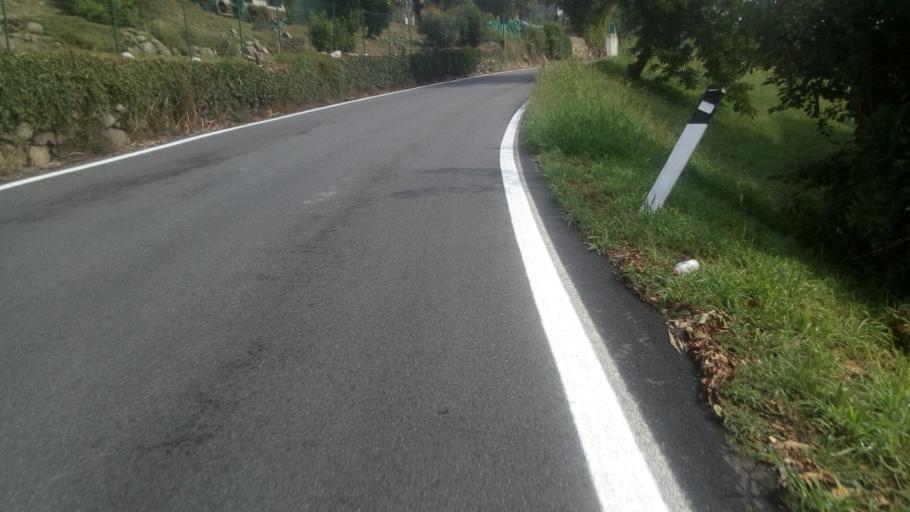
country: IT
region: Piedmont
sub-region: Provincia di Torino
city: Strambinello
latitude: 45.4230
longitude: 7.7711
